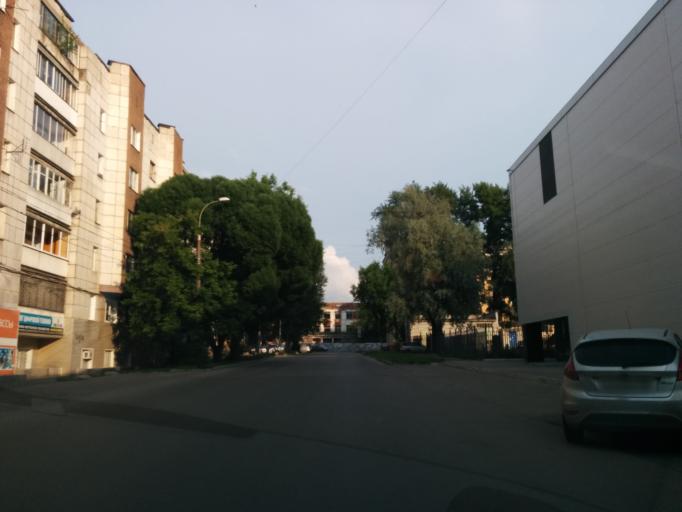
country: RU
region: Perm
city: Perm
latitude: 58.0270
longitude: 56.2954
